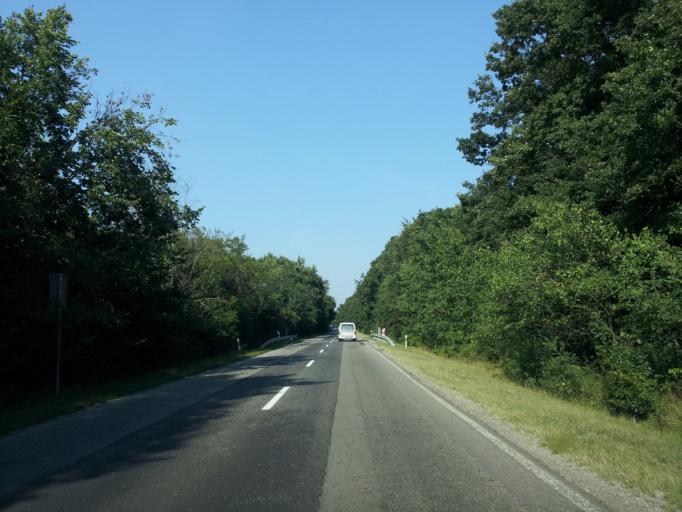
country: HU
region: Fejer
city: Polgardi
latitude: 47.0249
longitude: 18.2847
